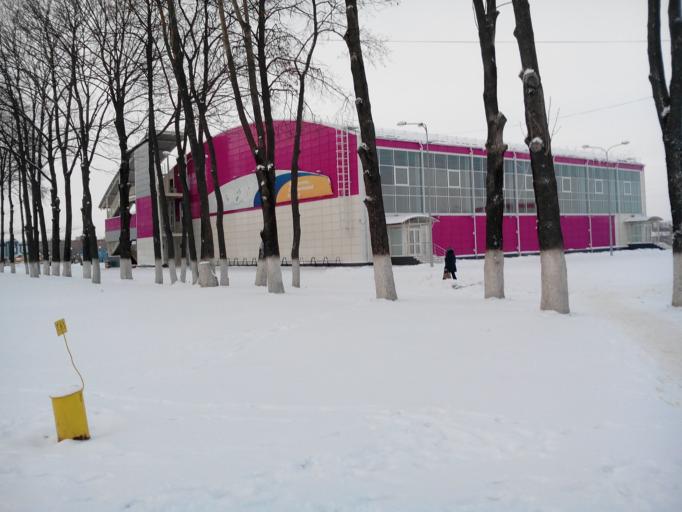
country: RU
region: Tula
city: Yefremov
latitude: 53.1467
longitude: 38.0936
